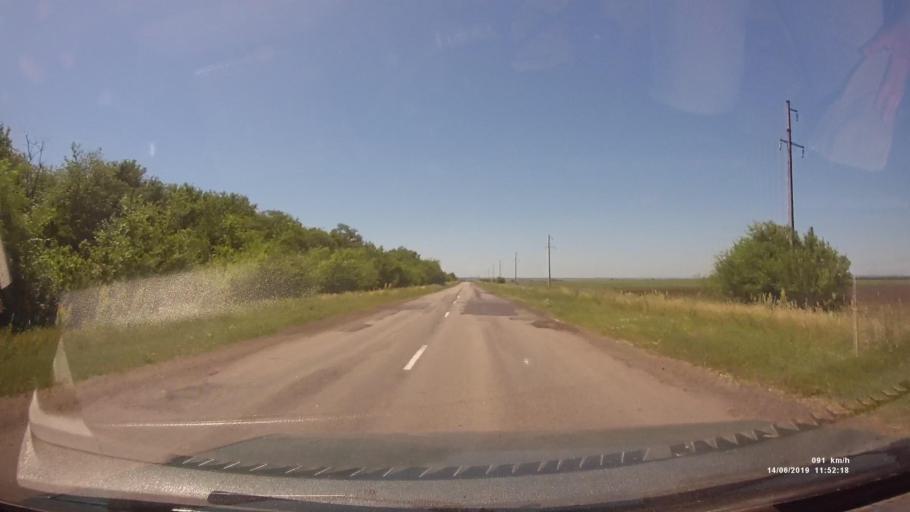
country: RU
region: Rostov
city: Kazanskaya
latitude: 49.8366
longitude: 41.2307
